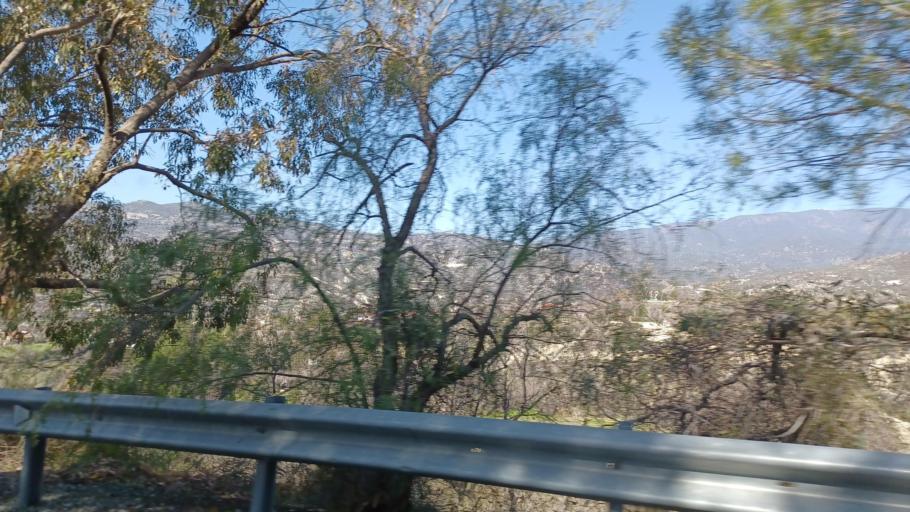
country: CY
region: Limassol
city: Pelendri
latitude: 34.8211
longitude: 32.9155
